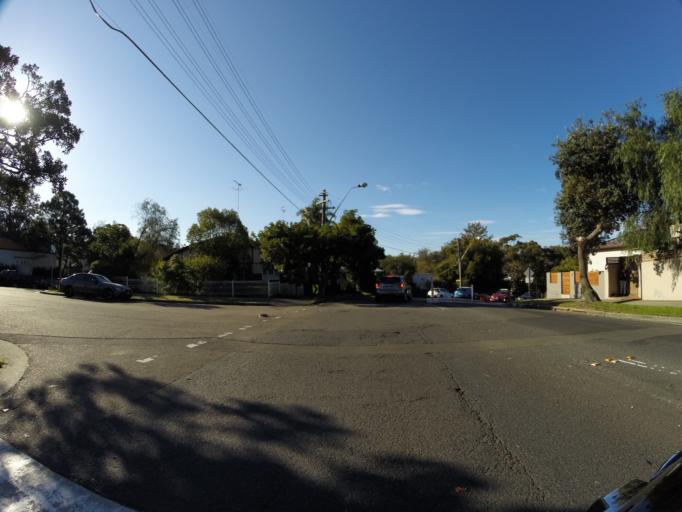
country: AU
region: New South Wales
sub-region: Waverley
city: Bronte
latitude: -33.9022
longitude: 151.2598
